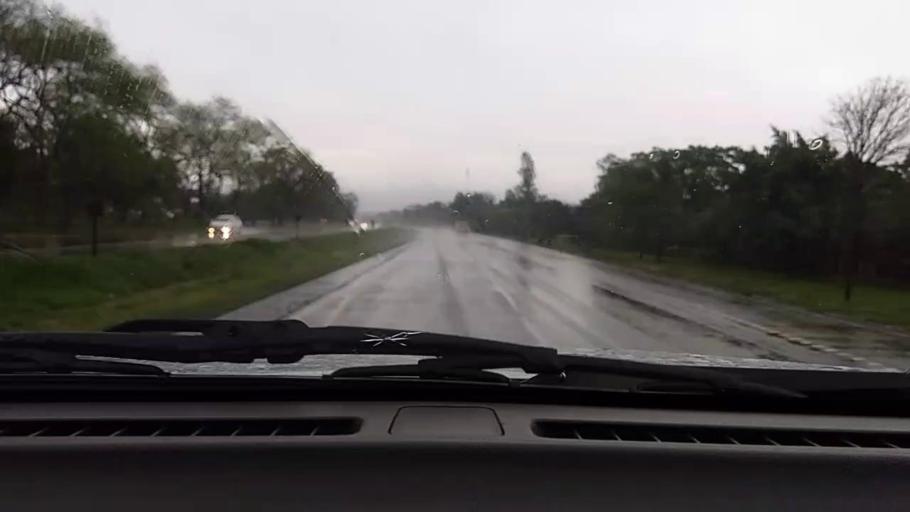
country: PY
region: Caaguazu
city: Repatriacion
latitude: -25.4556
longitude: -55.9135
